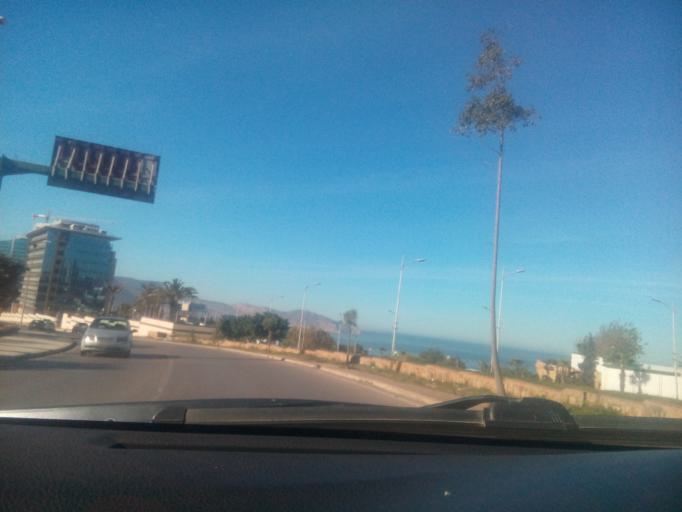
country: DZ
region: Oran
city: Oran
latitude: 35.7163
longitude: -0.6050
